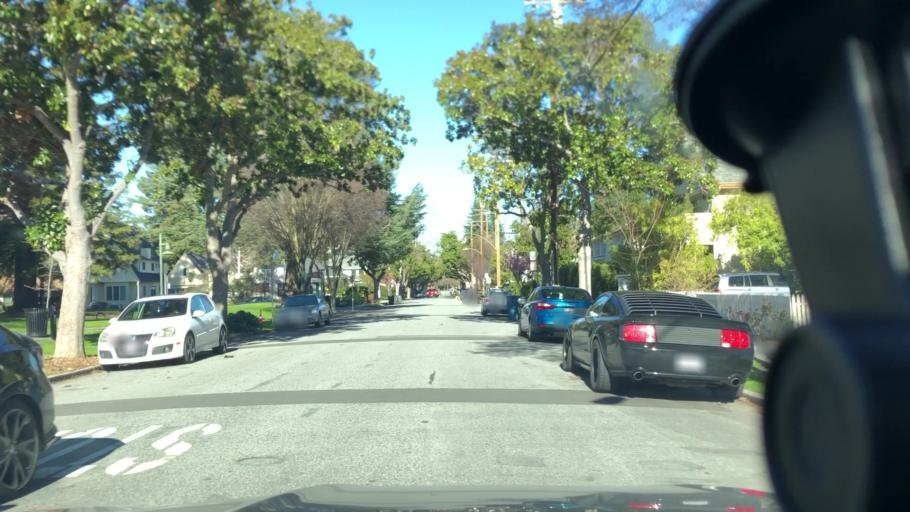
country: US
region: California
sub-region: San Mateo County
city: Menlo Park
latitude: 37.4488
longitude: -122.1629
